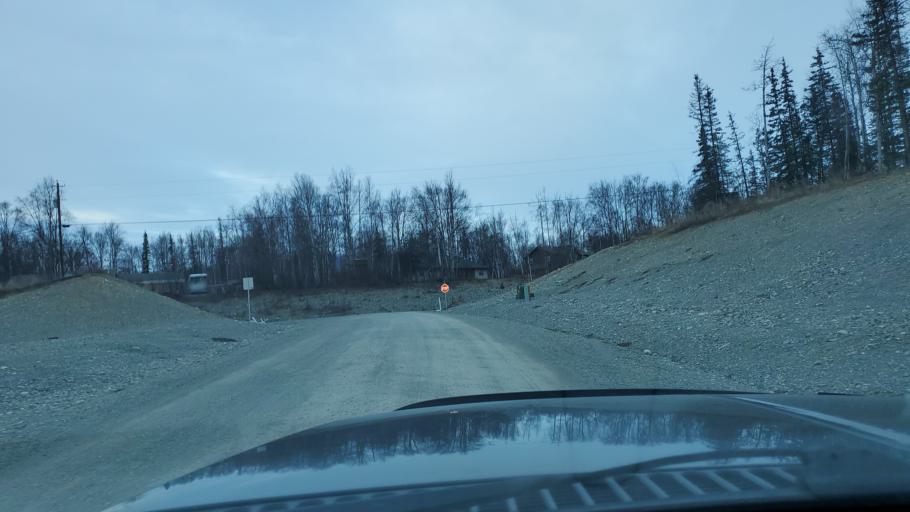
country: US
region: Alaska
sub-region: Matanuska-Susitna Borough
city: Lakes
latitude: 61.6565
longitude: -149.2904
